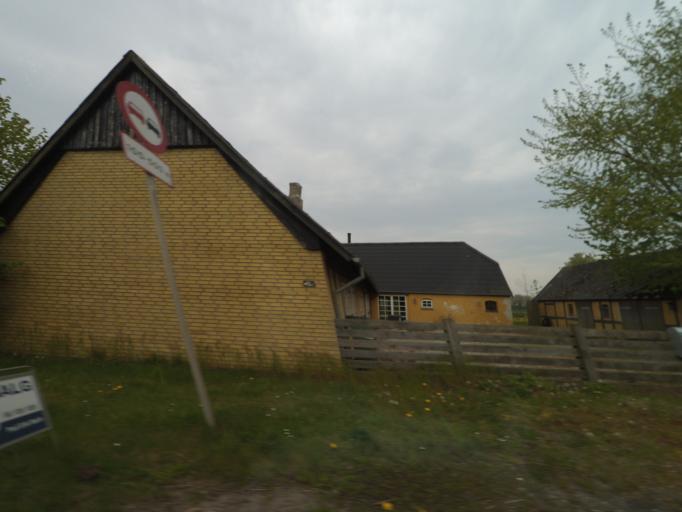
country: DK
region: South Denmark
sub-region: Faaborg-Midtfyn Kommune
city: Arslev
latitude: 55.3165
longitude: 10.4466
